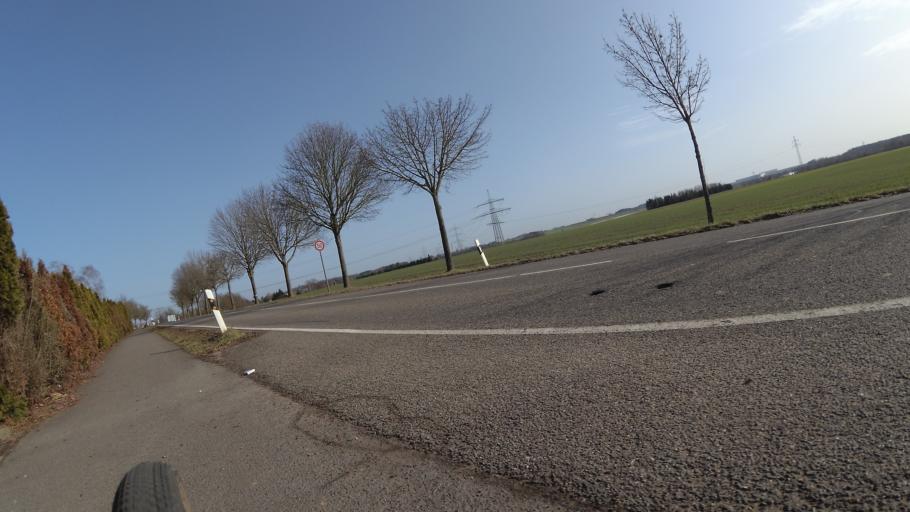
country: DE
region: Saarland
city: Uberherrn
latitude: 49.2776
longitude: 6.7192
